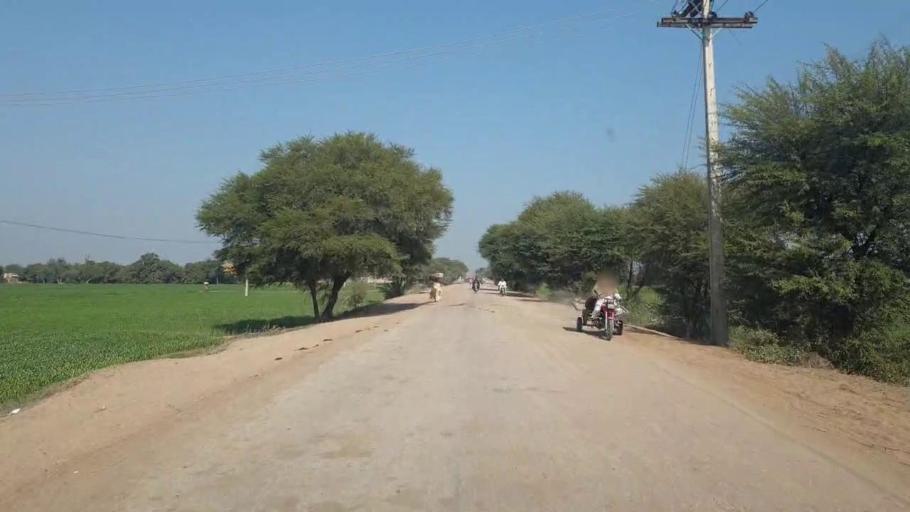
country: PK
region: Sindh
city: Sakrand
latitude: 26.0494
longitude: 68.4031
